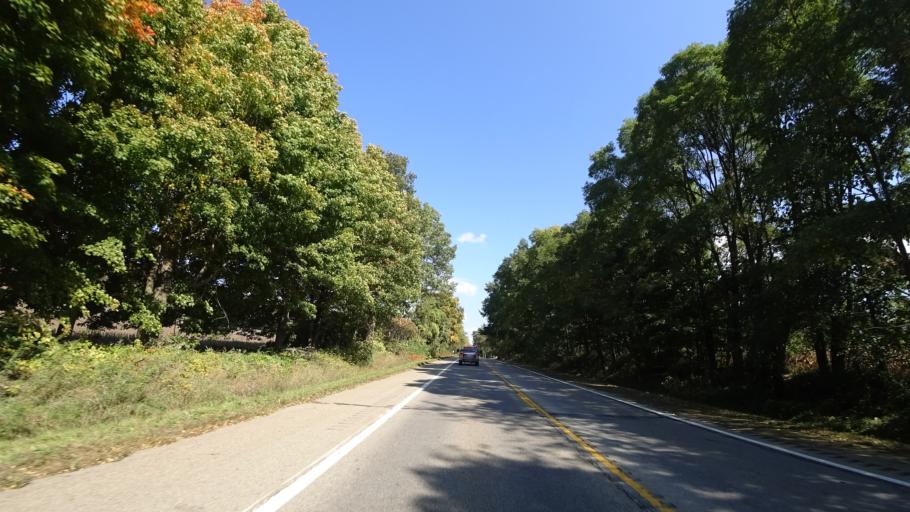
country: US
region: Michigan
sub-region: Calhoun County
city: Homer
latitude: 42.1533
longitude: -84.7861
